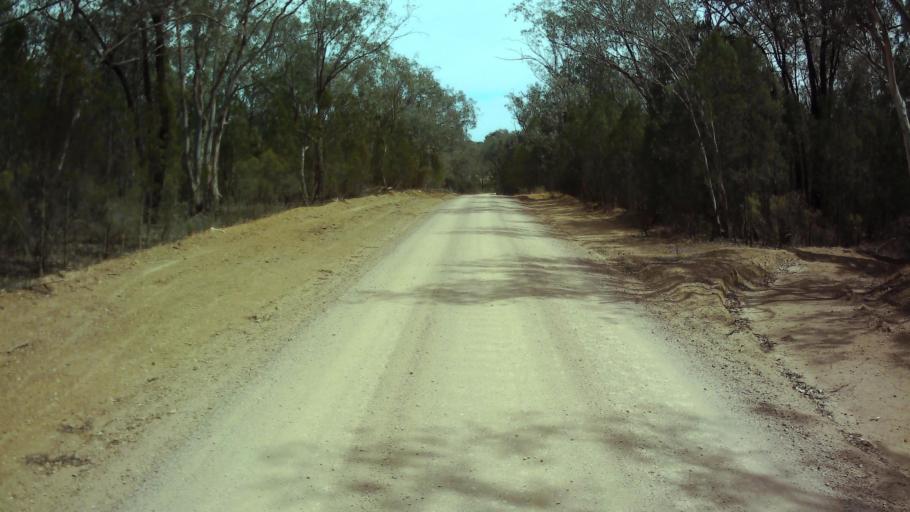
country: AU
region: New South Wales
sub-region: Weddin
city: Grenfell
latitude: -33.9204
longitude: 148.4147
